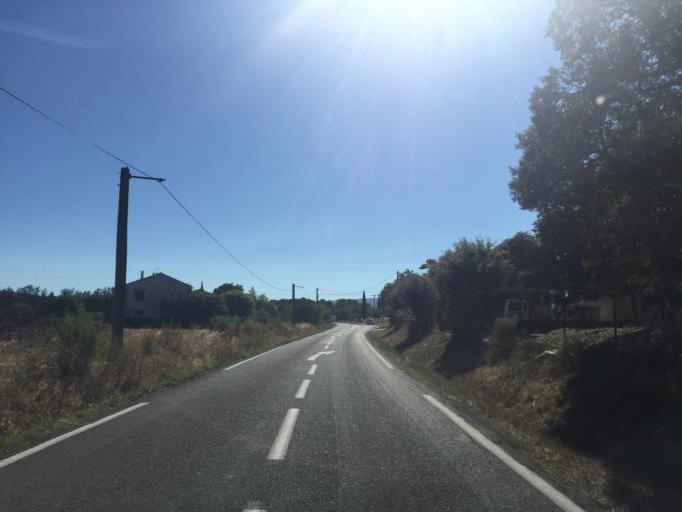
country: FR
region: Provence-Alpes-Cote d'Azur
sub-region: Departement du Vaucluse
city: Saint-Didier
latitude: 44.0254
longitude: 5.1044
